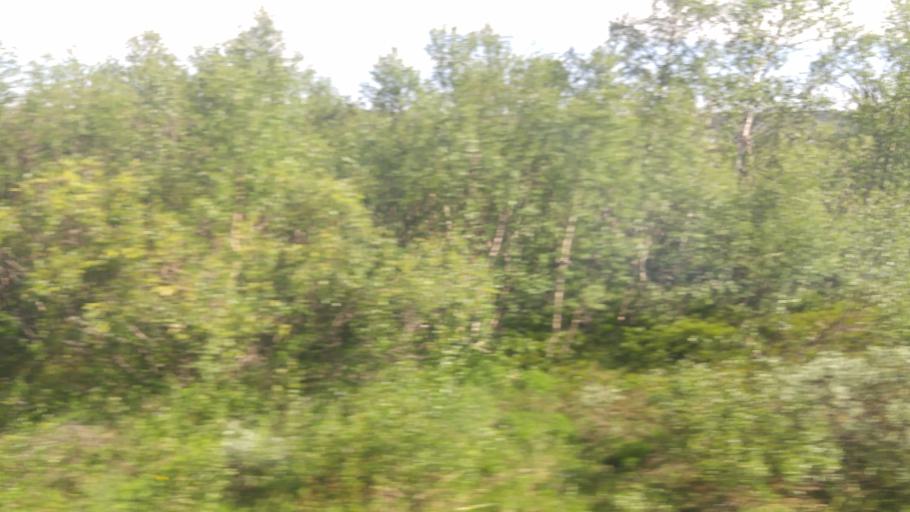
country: NO
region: Nord-Trondelag
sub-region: Meraker
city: Meraker
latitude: 63.3156
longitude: 12.2187
